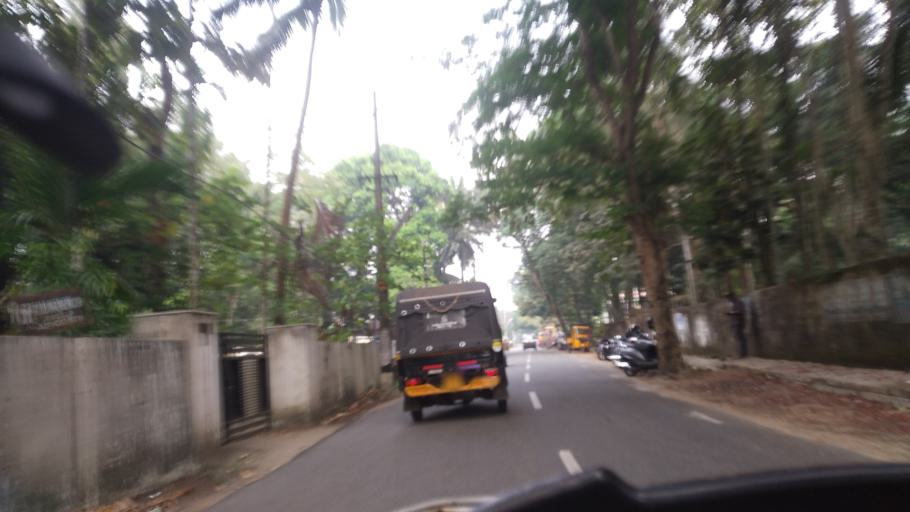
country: IN
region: Kerala
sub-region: Ernakulam
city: Elur
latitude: 10.1451
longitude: 76.2442
